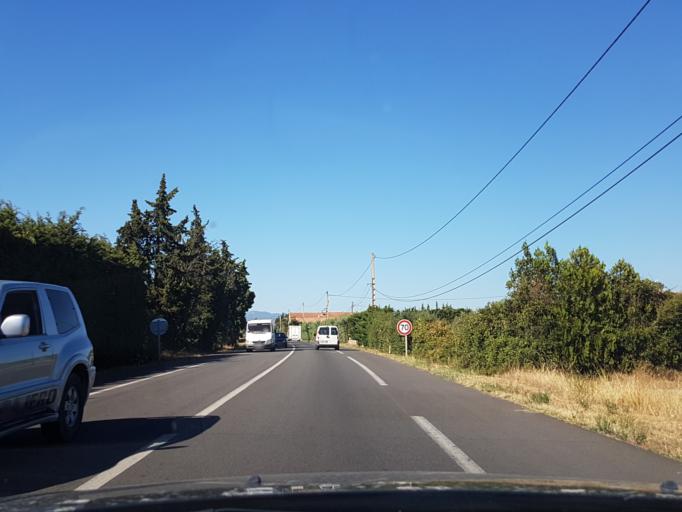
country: FR
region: Provence-Alpes-Cote d'Azur
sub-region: Departement du Vaucluse
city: Pernes-les-Fontaines
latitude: 44.0234
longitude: 5.0367
